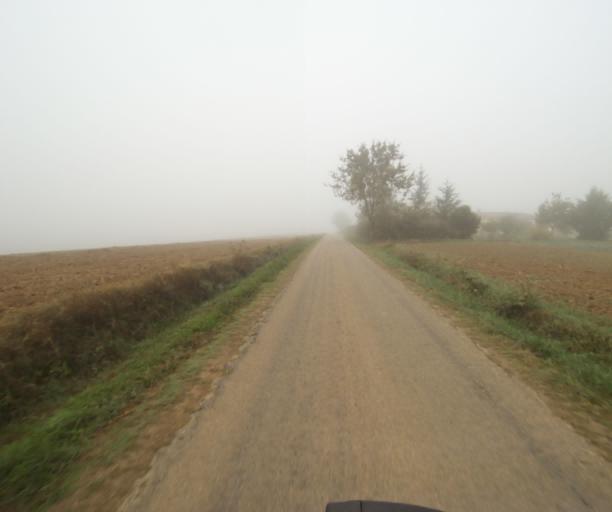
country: FR
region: Midi-Pyrenees
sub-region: Departement du Tarn-et-Garonne
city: Nohic
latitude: 43.9308
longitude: 1.4712
